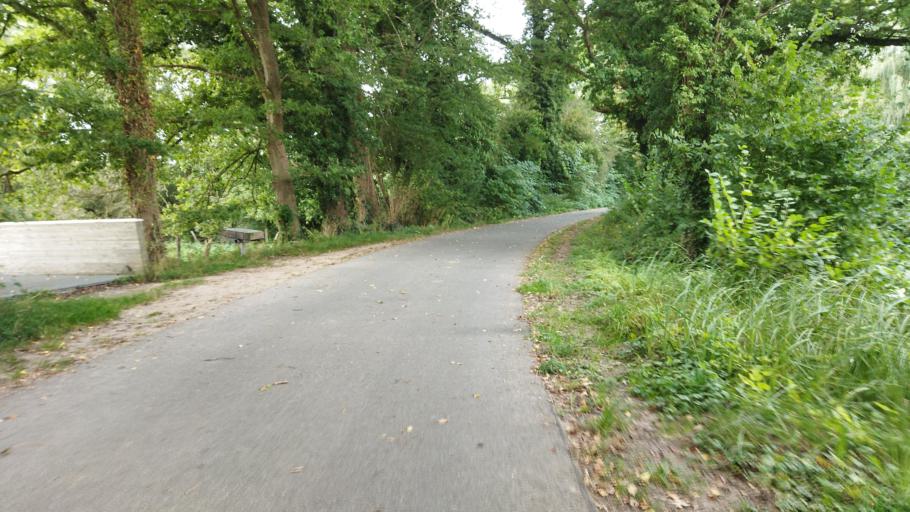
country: DE
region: North Rhine-Westphalia
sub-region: Regierungsbezirk Munster
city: Telgte
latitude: 52.0161
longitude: 7.7622
